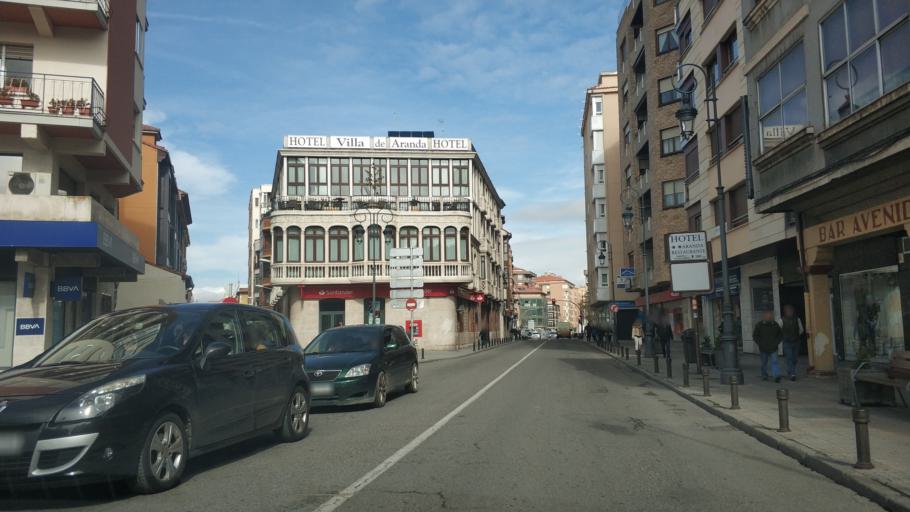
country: ES
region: Castille and Leon
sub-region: Provincia de Burgos
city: Aranda de Duero
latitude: 41.6717
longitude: -3.6851
